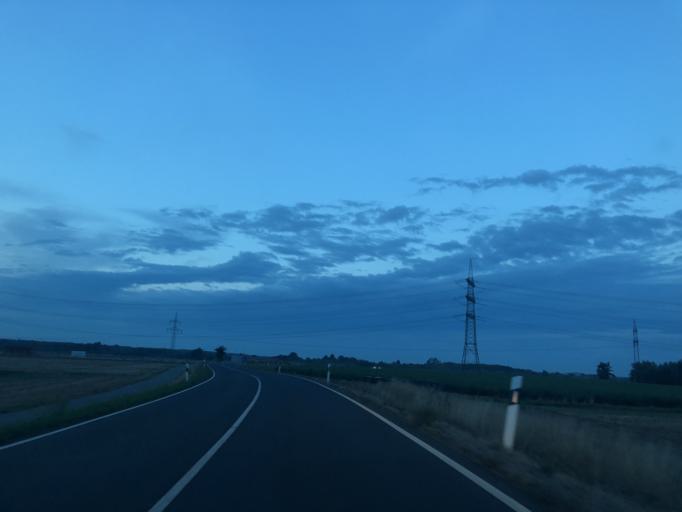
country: DE
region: Hesse
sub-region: Regierungsbezirk Darmstadt
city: Trebur
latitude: 49.9284
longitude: 8.4323
